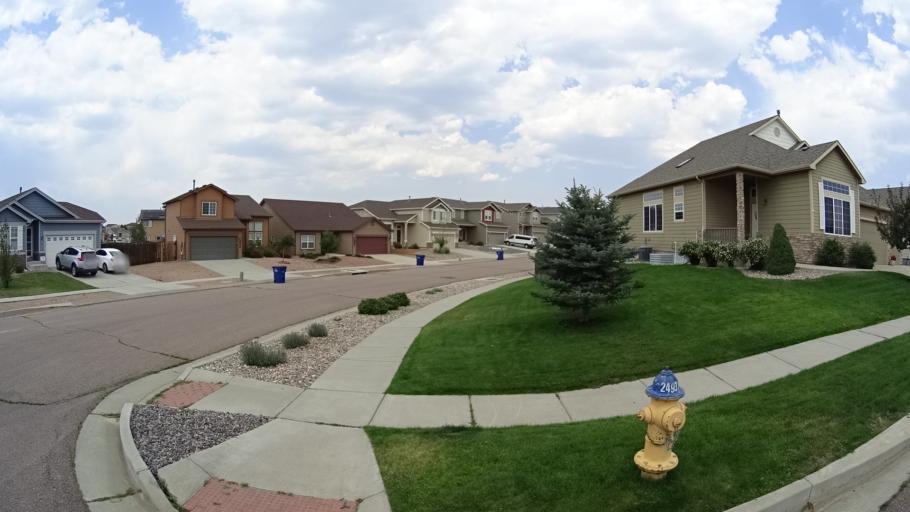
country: US
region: Colorado
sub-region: El Paso County
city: Black Forest
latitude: 38.9449
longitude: -104.6938
